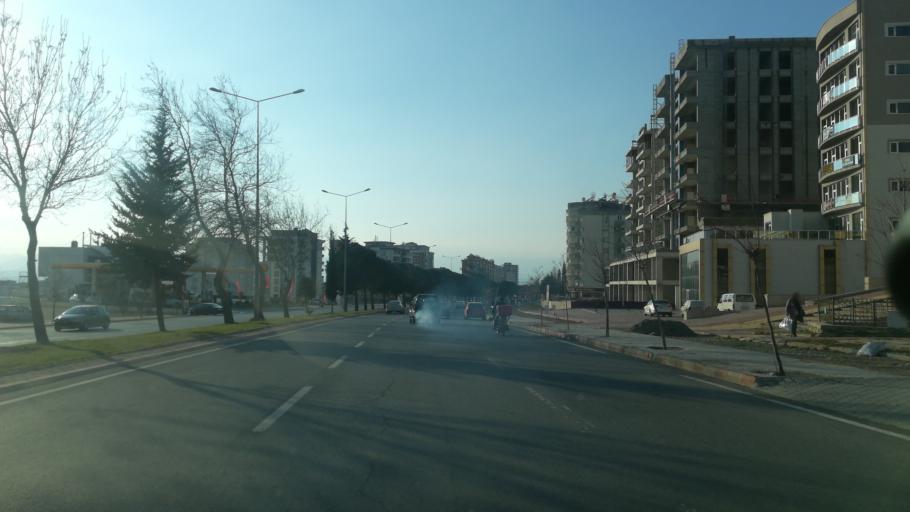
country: TR
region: Kahramanmaras
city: Kahramanmaras
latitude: 37.5933
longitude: 36.8591
